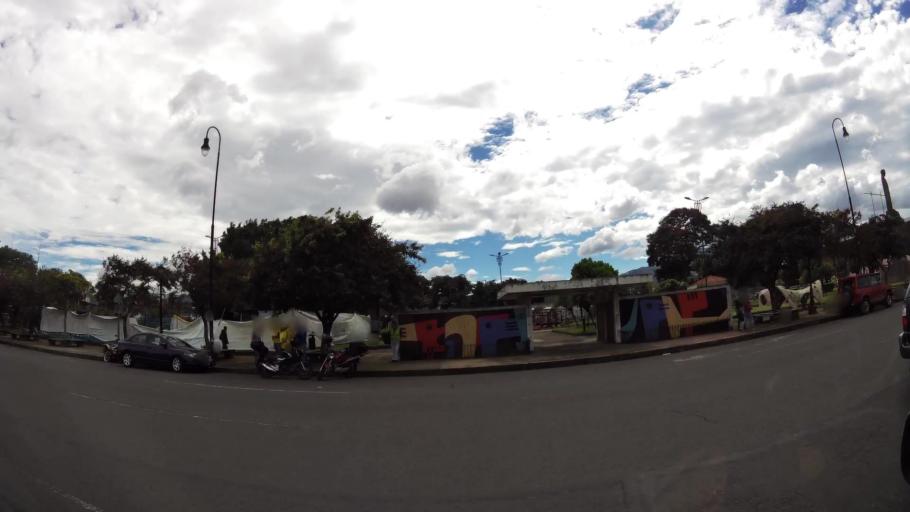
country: CR
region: San Jose
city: San Jose
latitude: 9.9257
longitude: -84.0742
